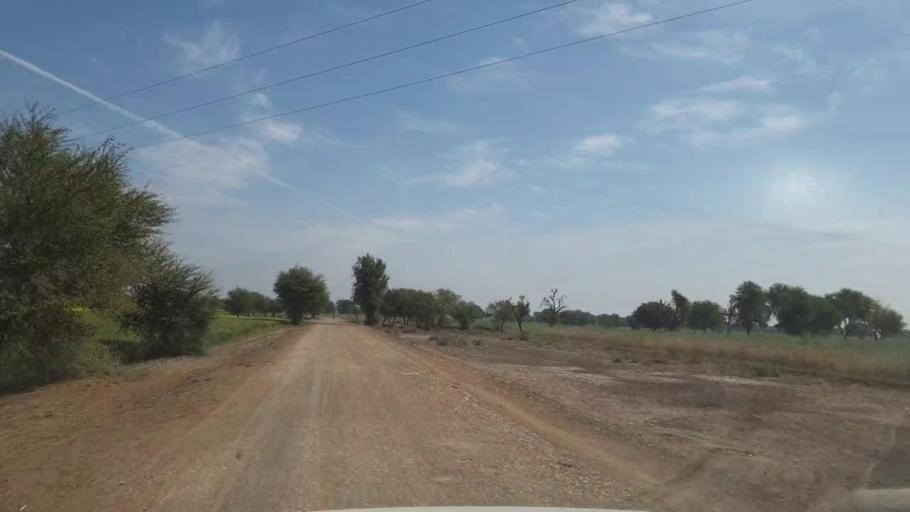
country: PK
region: Sindh
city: Mirpur Khas
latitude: 25.6268
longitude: 69.1998
